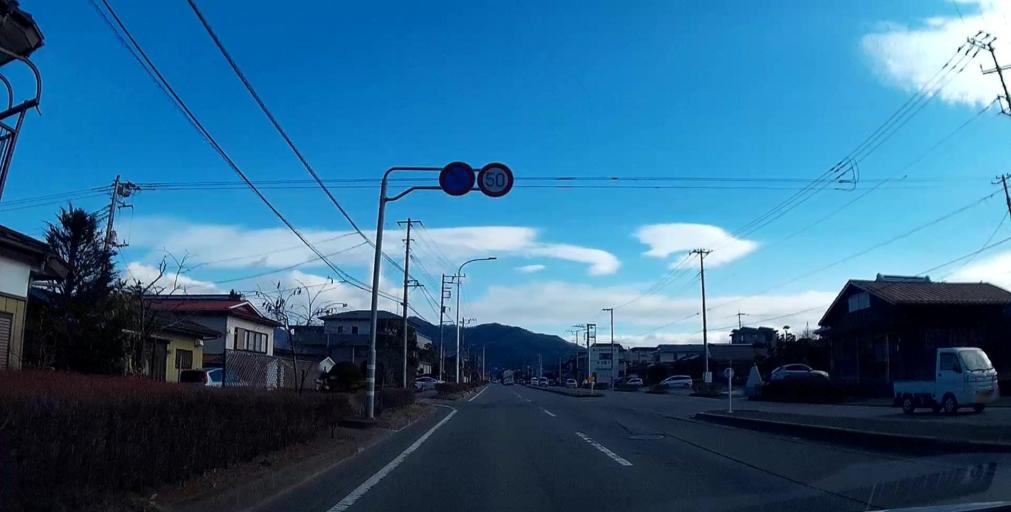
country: JP
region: Yamanashi
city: Fujikawaguchiko
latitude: 35.4885
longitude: 138.7969
